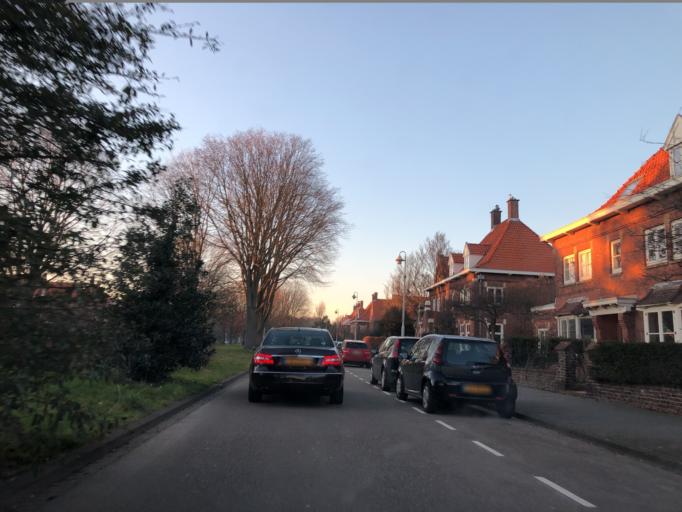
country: NL
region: South Holland
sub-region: Gemeente Den Haag
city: Scheveningen
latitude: 52.0787
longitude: 4.2537
